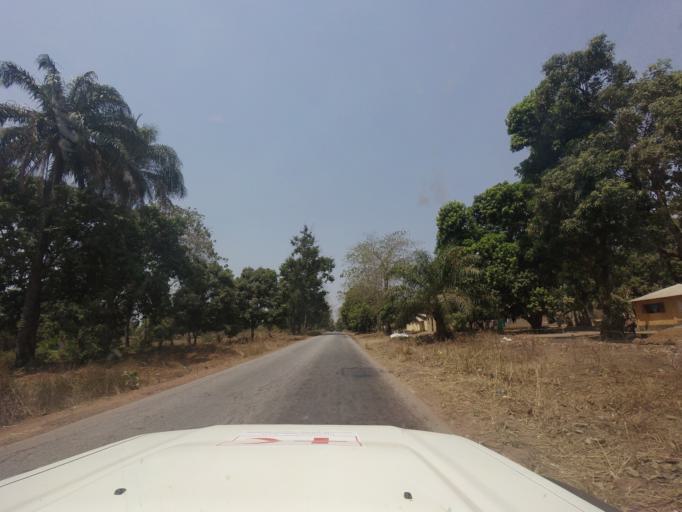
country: GN
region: Kindia
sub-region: Kindia
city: Kindia
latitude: 9.9360
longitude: -12.9802
